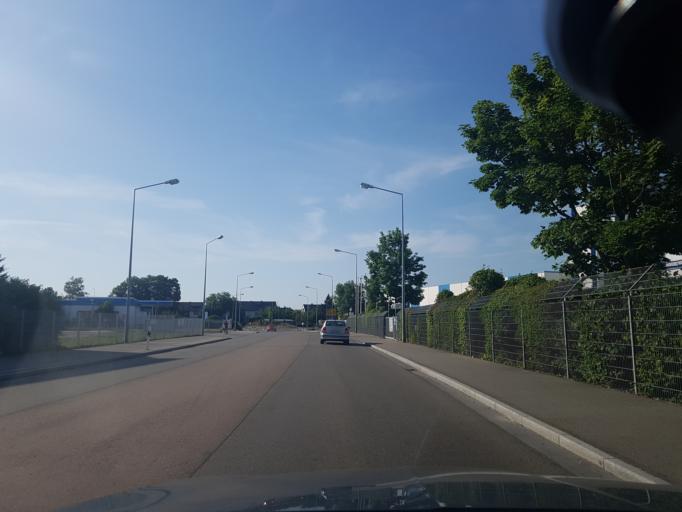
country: DE
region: Bavaria
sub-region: Swabia
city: Leipheim
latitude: 48.4447
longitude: 10.2141
